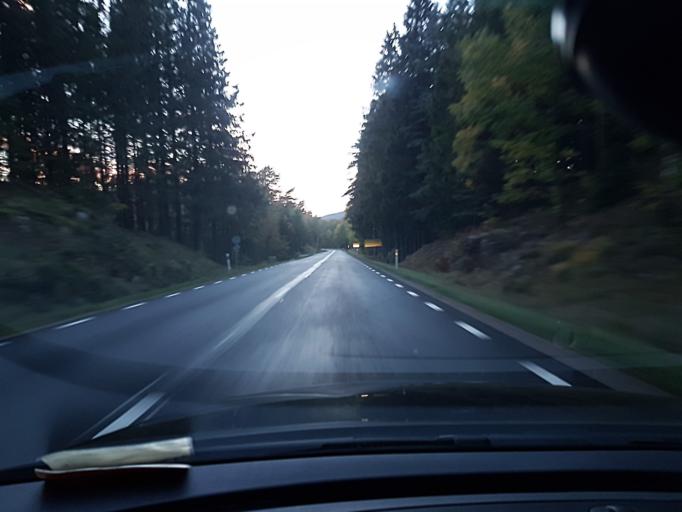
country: SE
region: Halland
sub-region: Laholms Kommun
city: Veinge
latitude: 56.7217
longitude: 13.1660
